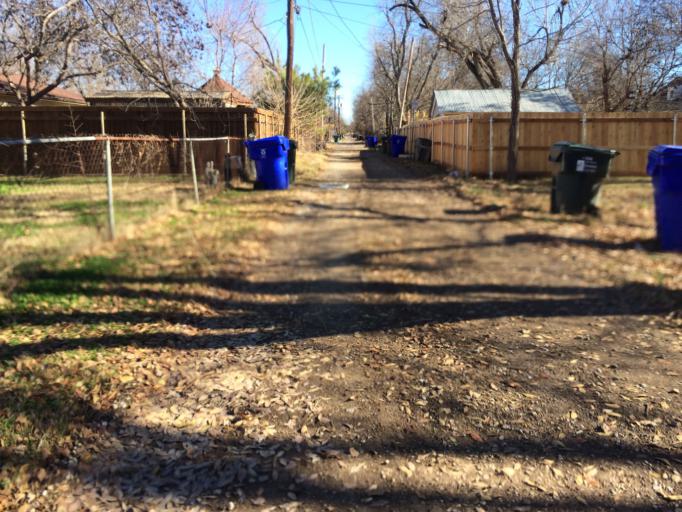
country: US
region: Oklahoma
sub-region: Cleveland County
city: Norman
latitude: 35.2236
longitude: -97.4539
